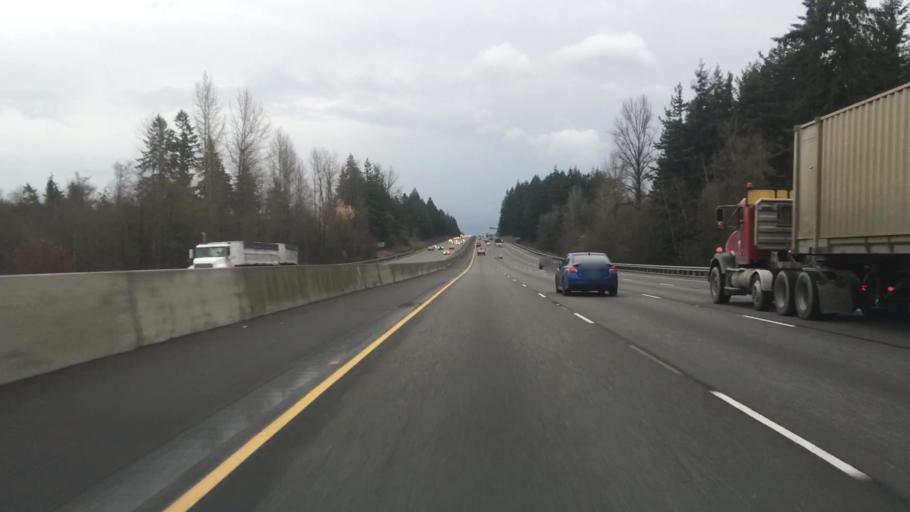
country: US
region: Washington
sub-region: Thurston County
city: Grand Mound
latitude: 46.8888
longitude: -122.9634
